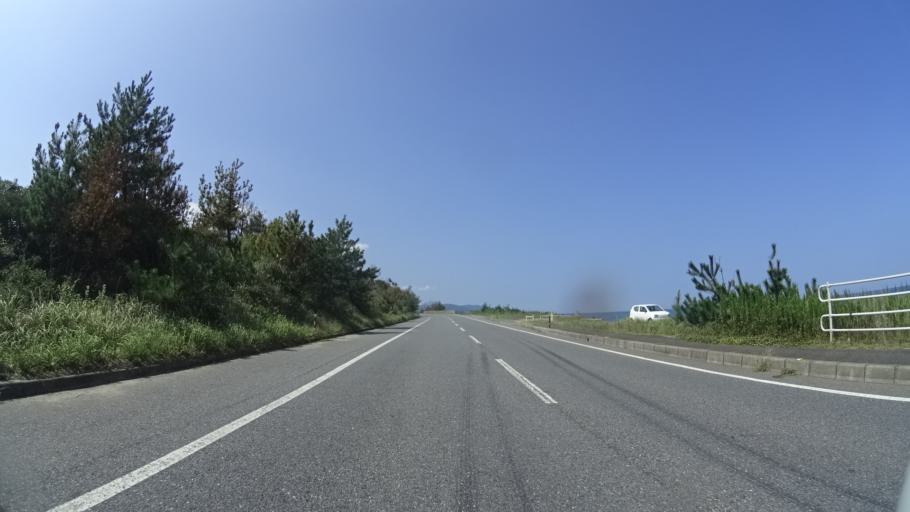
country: JP
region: Shimane
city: Masuda
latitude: 34.6830
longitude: 131.7783
